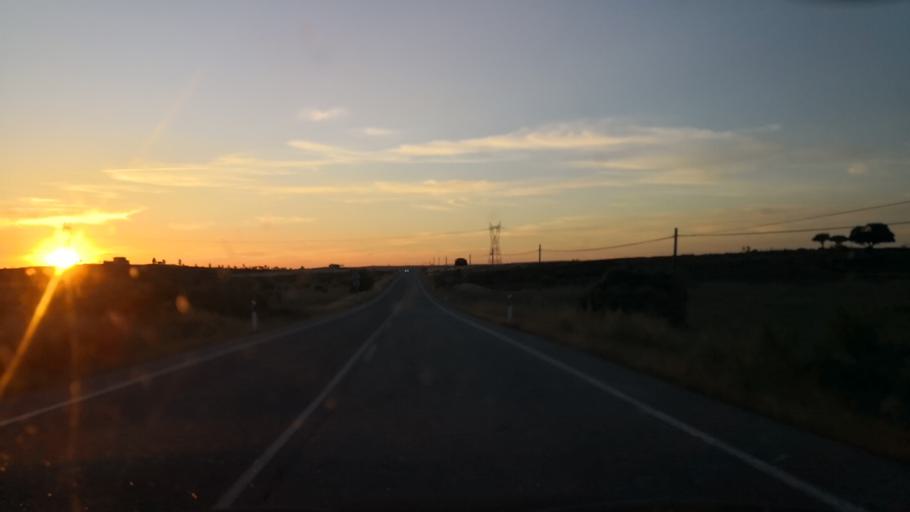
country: ES
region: Extremadura
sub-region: Provincia de Caceres
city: Alcantara
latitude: 39.6964
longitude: -6.8718
